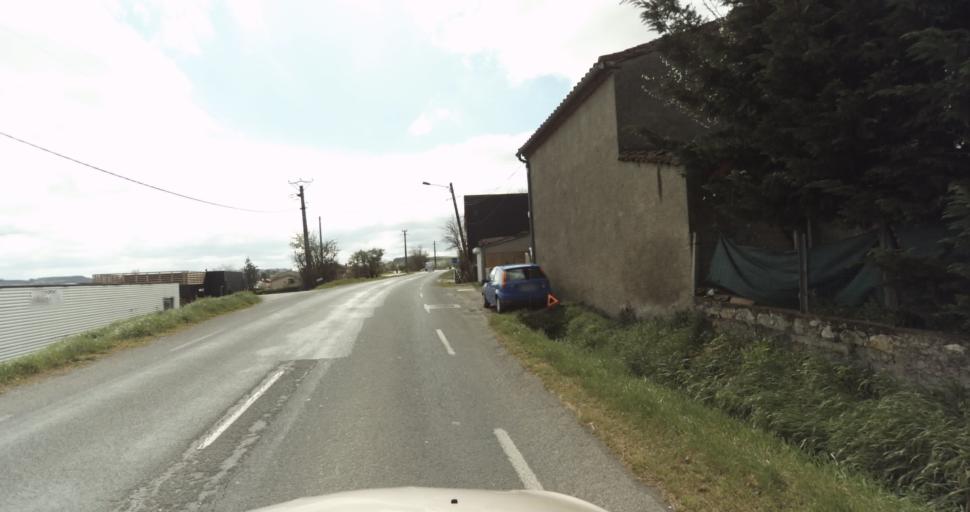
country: FR
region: Midi-Pyrenees
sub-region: Departement du Tarn
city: Puygouzon
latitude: 43.8968
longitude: 2.1505
